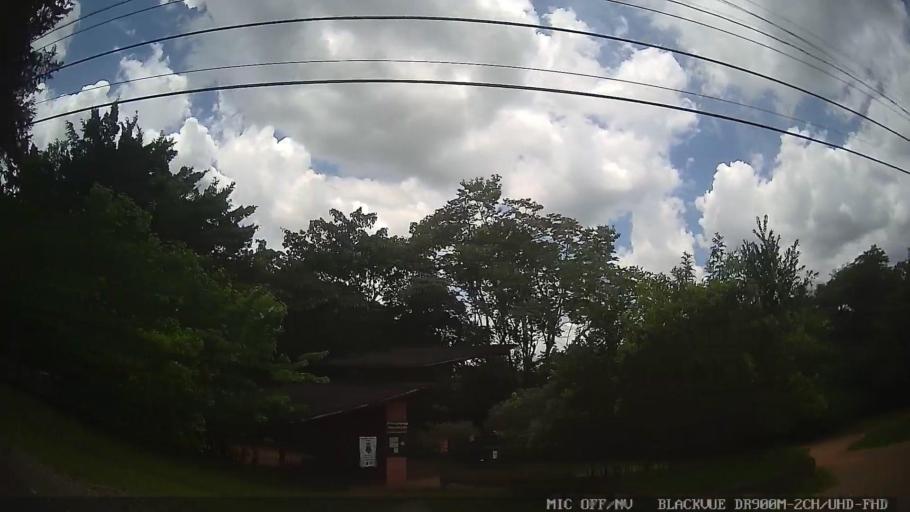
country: BR
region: Sao Paulo
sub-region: Jarinu
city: Jarinu
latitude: -23.0780
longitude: -46.6419
